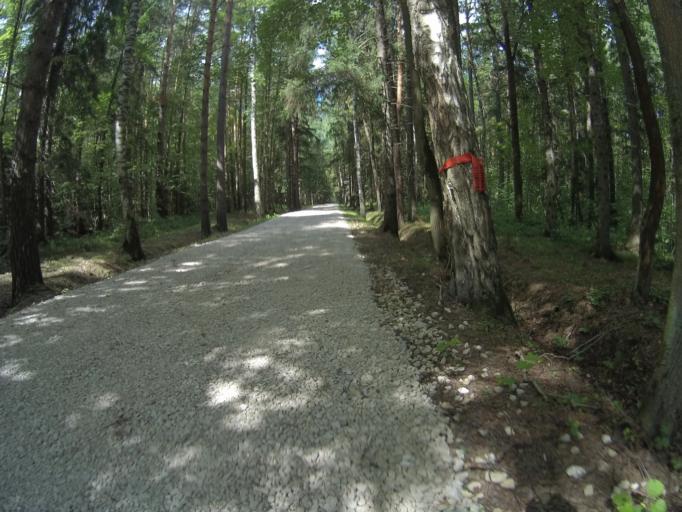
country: RU
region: Vladimir
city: Raduzhnyy
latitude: 56.0567
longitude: 40.2927
